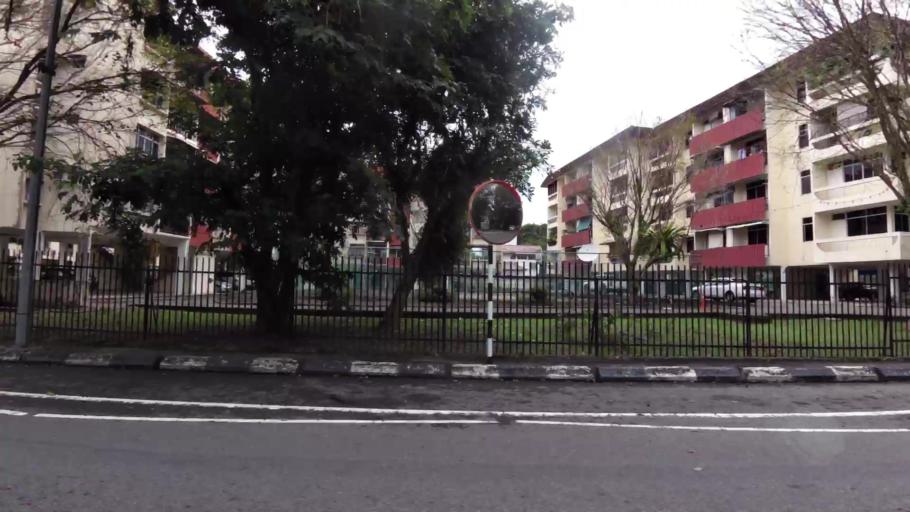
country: BN
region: Brunei and Muara
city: Bandar Seri Begawan
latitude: 4.8956
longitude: 114.9392
